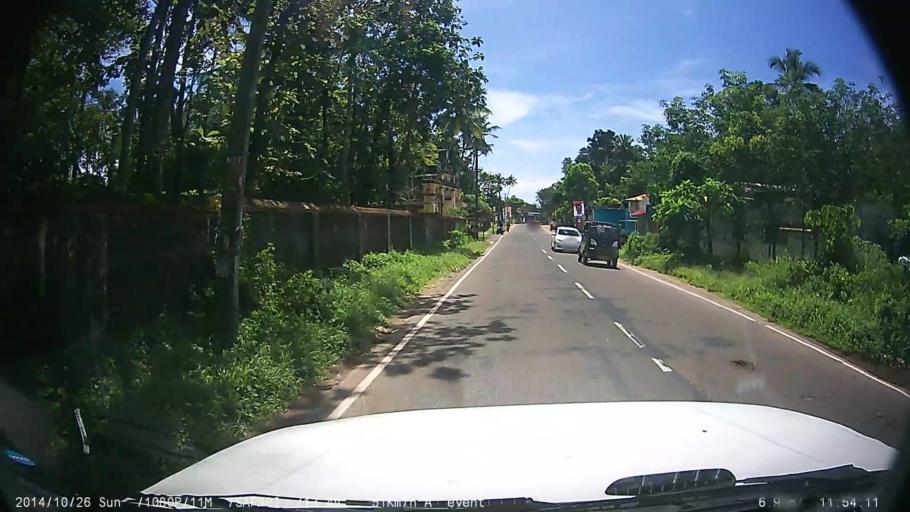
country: IN
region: Kerala
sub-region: Kottayam
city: Palackattumala
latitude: 9.7375
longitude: 76.5615
